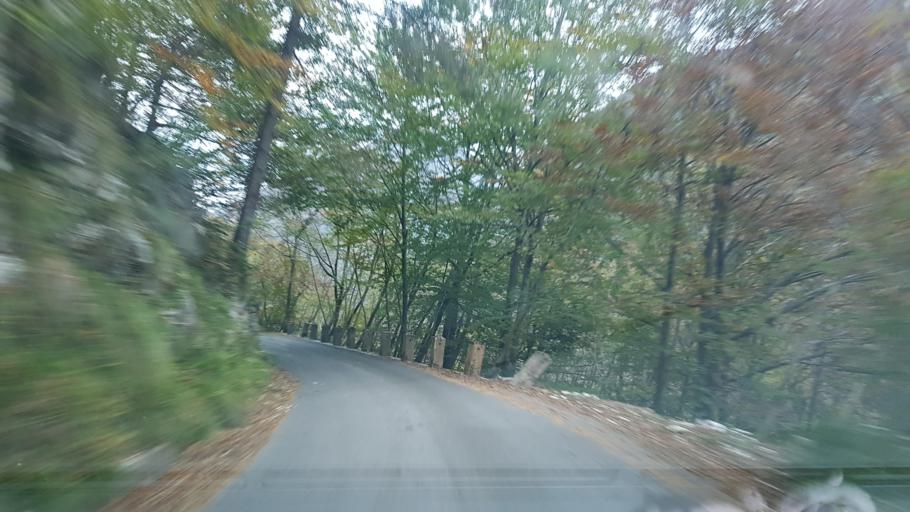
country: IT
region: Friuli Venezia Giulia
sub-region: Provincia di Udine
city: Preone
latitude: 46.3460
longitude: 12.8956
